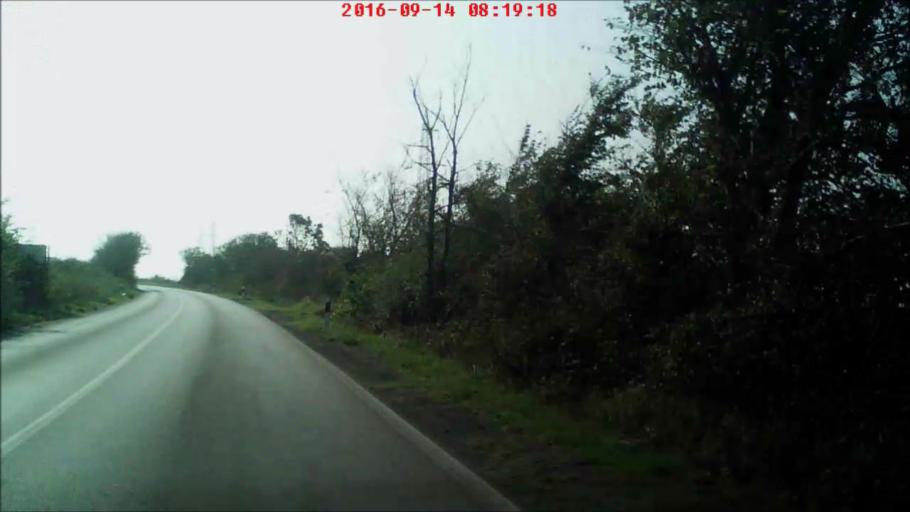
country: HR
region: Zadarska
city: Nin
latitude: 44.2337
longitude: 15.1887
